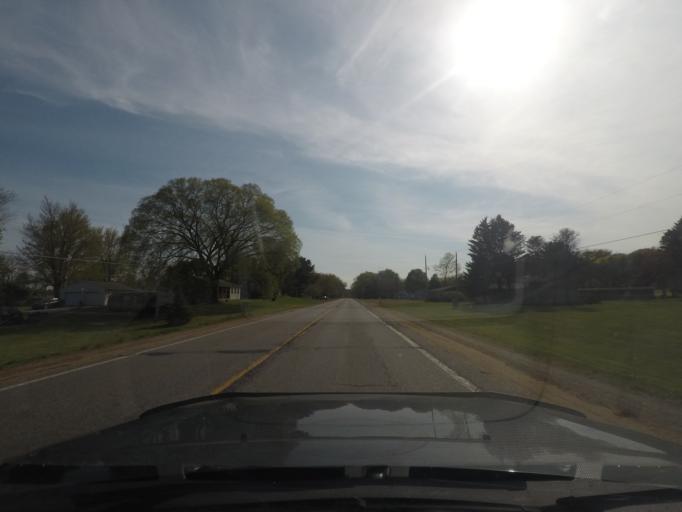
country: US
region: Michigan
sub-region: Berrien County
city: Buchanan
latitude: 41.7979
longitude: -86.4126
